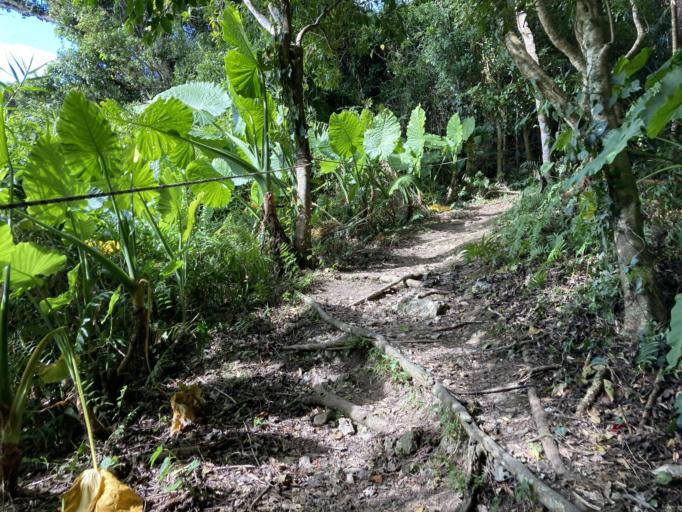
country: JP
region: Okinawa
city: Tomigusuku
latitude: 26.1431
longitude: 127.7820
